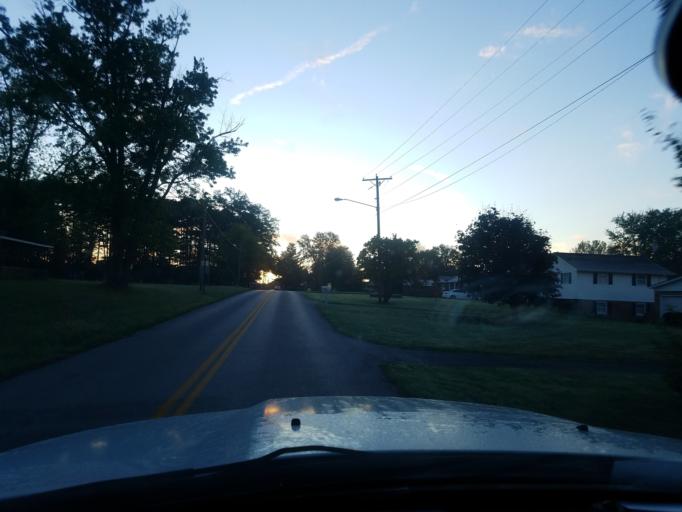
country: US
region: Kentucky
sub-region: Laurel County
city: London
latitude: 37.0954
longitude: -84.0708
